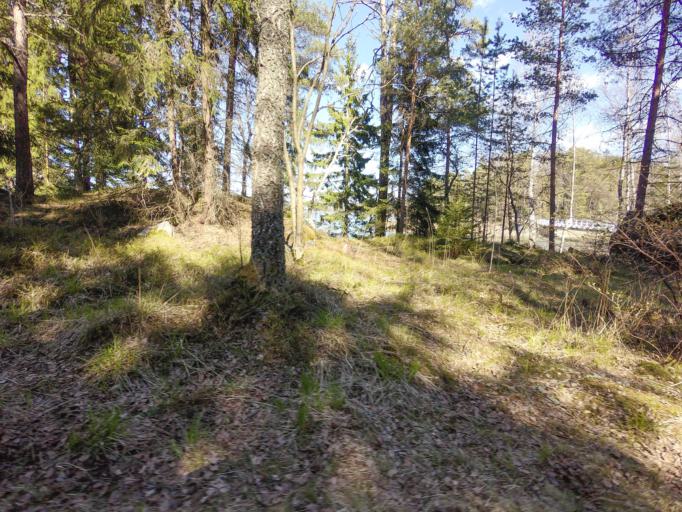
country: FI
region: Uusimaa
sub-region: Helsinki
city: Vantaa
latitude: 60.1698
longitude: 25.0671
